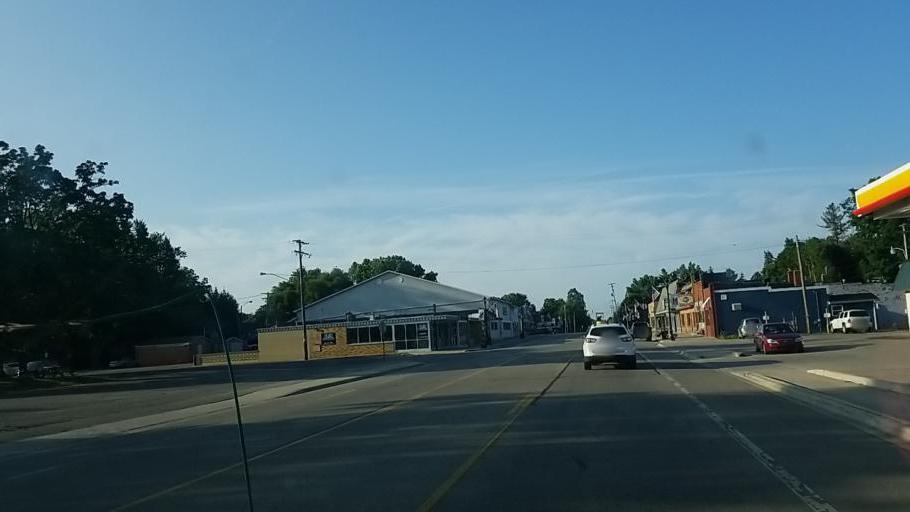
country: US
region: Michigan
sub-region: Montcalm County
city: Stanton
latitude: 43.2131
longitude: -85.0736
